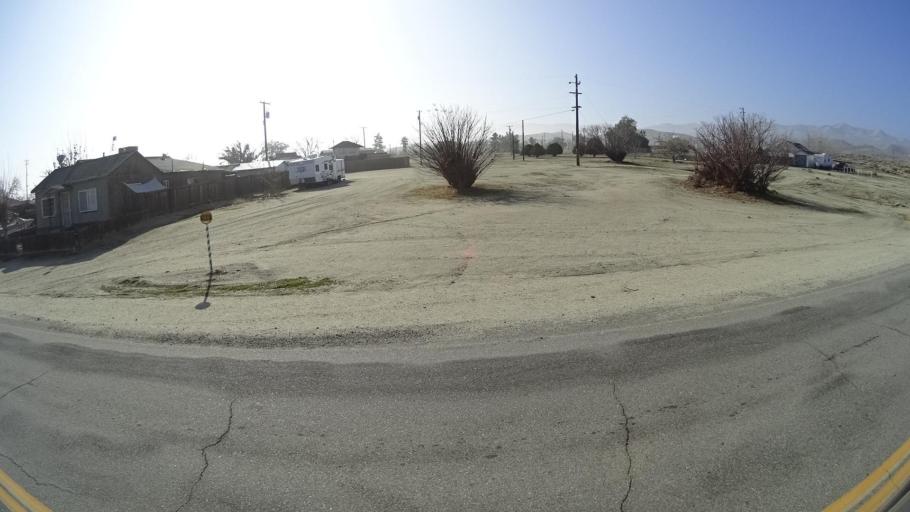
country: US
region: California
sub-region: Kern County
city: Taft Heights
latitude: 35.1795
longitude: -119.5439
